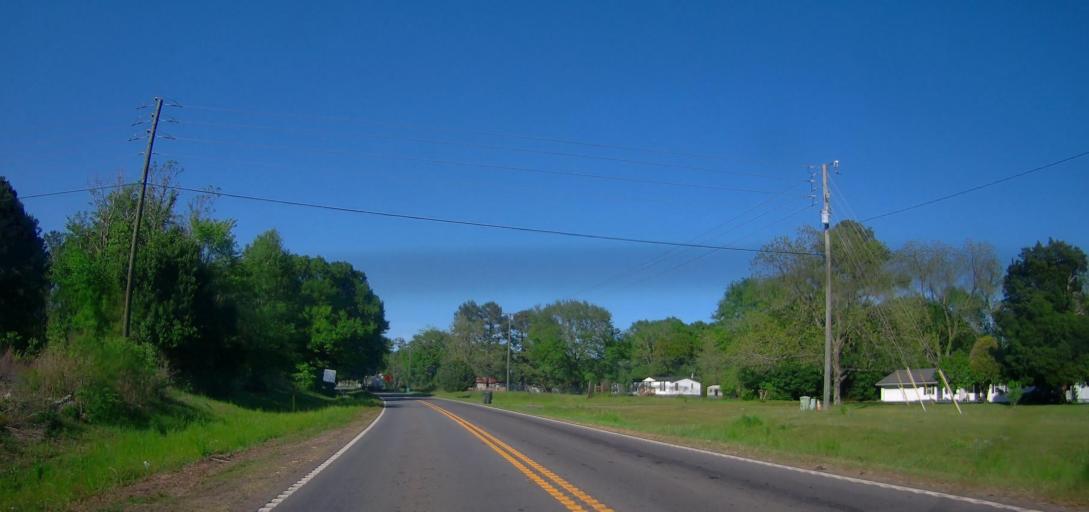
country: US
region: Georgia
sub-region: Houston County
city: Perry
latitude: 32.4551
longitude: -83.6198
